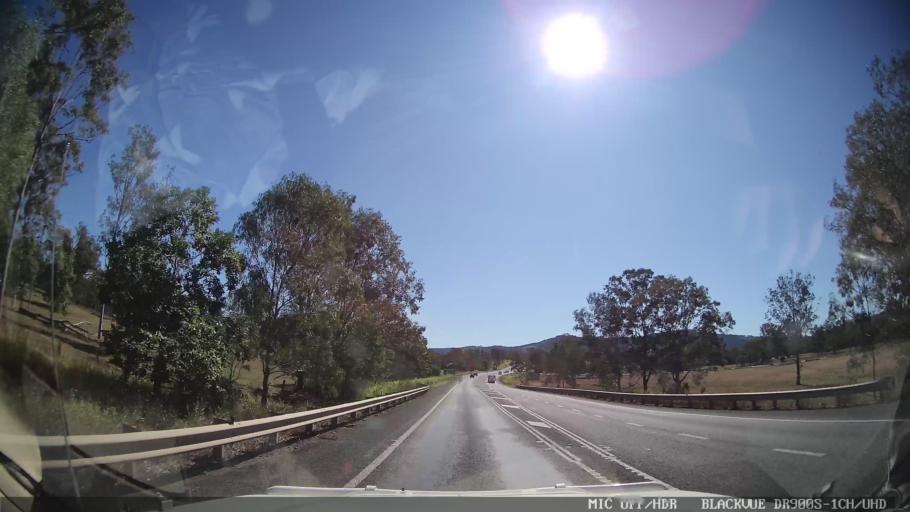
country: AU
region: Queensland
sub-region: Gympie Regional Council
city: Gympie
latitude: -25.9980
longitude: 152.5663
